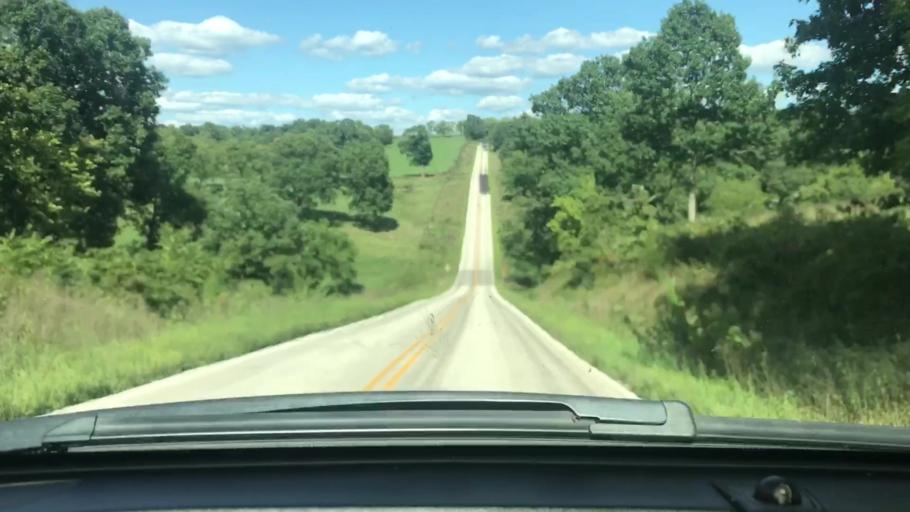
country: US
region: Missouri
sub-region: Wright County
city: Hartville
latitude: 37.3730
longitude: -92.3867
